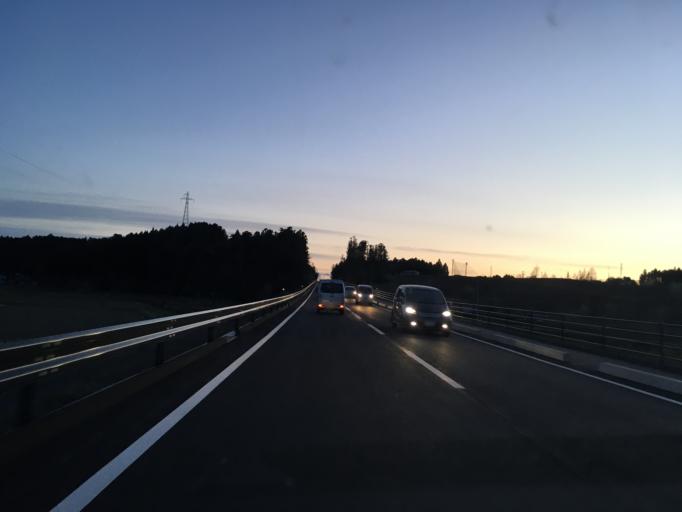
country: JP
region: Miyagi
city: Wakuya
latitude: 38.7279
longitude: 141.2843
